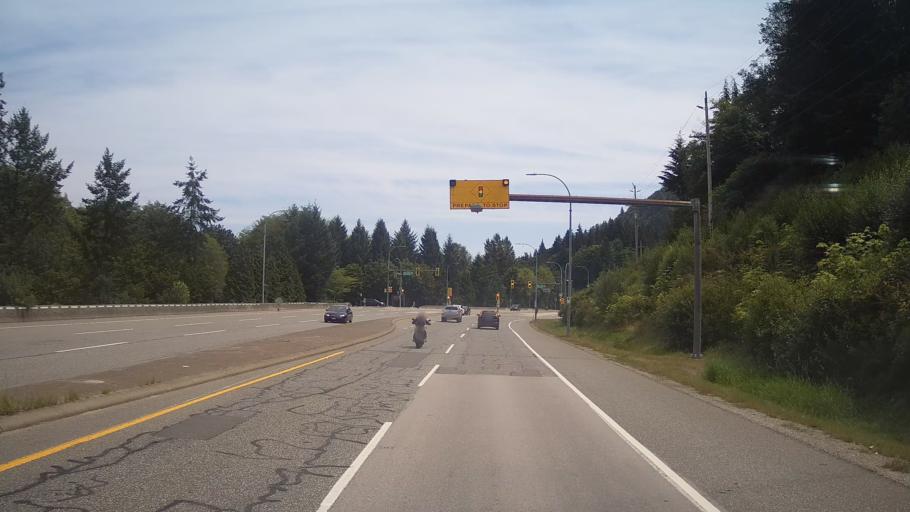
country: CA
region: British Columbia
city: Burnaby
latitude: 49.2894
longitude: -122.9278
